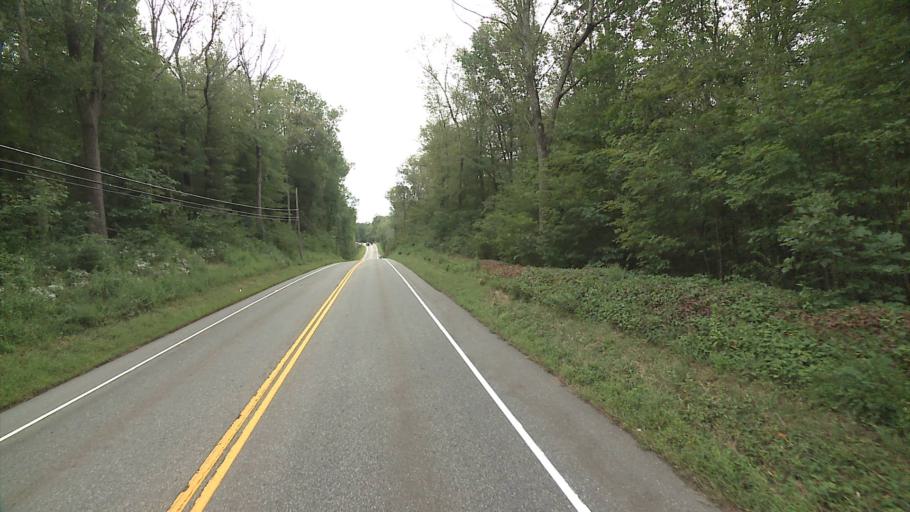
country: US
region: Connecticut
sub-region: Hartford County
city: Terramuggus
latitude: 41.7238
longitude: -72.4361
